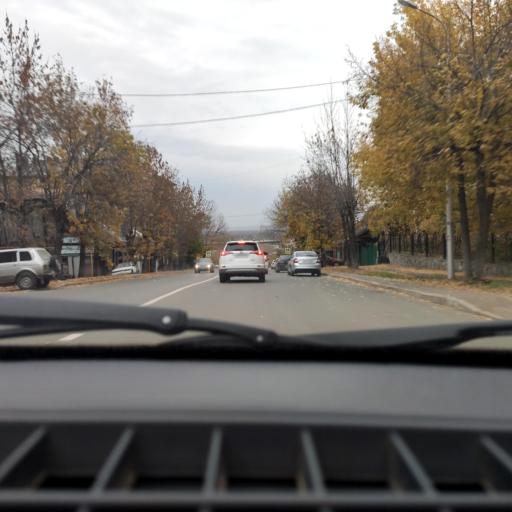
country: RU
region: Bashkortostan
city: Ufa
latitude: 54.7488
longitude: 55.9608
